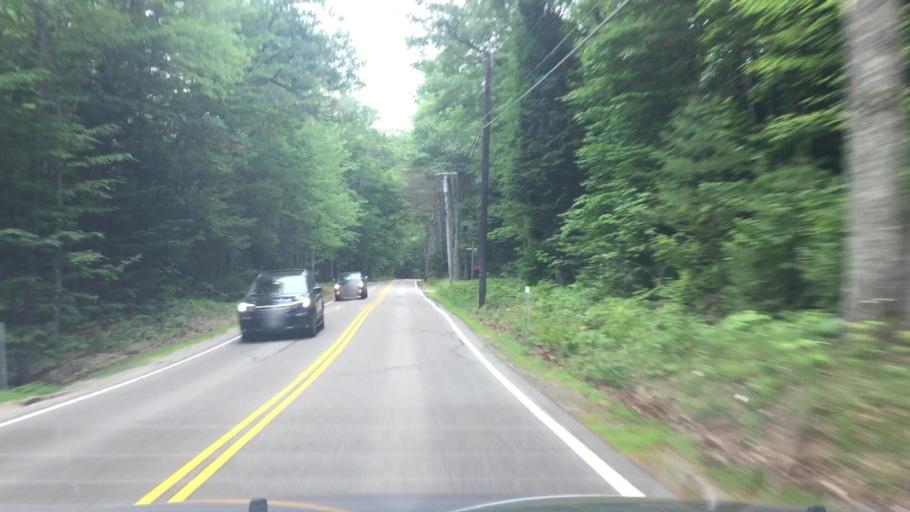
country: US
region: New Hampshire
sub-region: Carroll County
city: Madison
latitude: 43.8977
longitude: -71.0719
